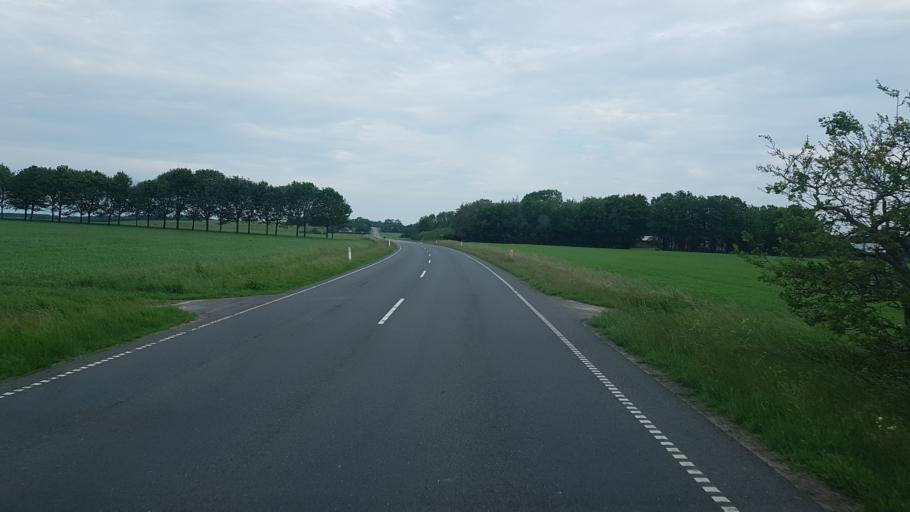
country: DK
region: South Denmark
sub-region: Vejen Kommune
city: Rodding
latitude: 55.4090
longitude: 9.0321
